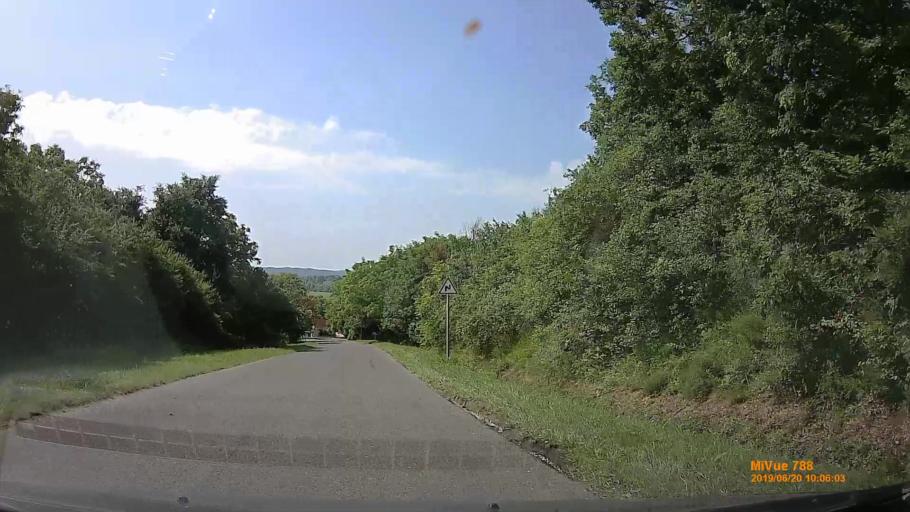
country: HU
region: Baranya
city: Mecseknadasd
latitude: 46.1882
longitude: 18.4808
